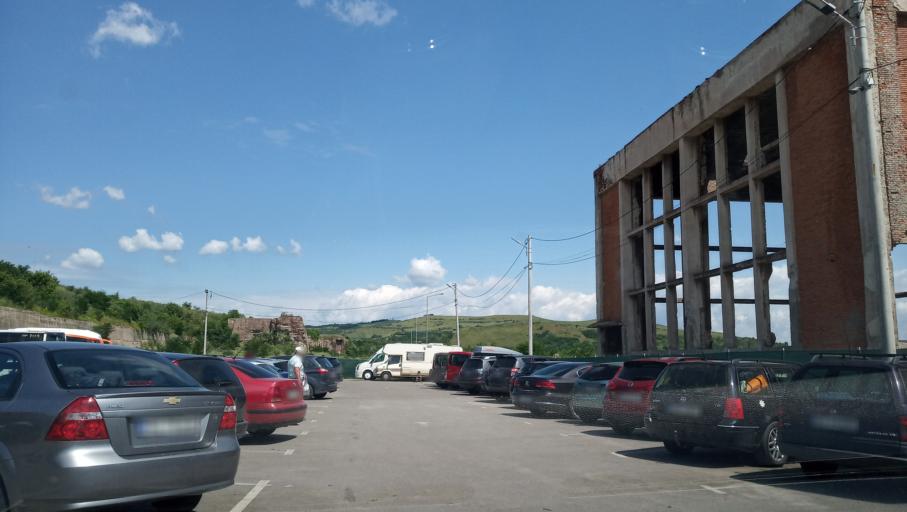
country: RO
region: Hunedoara
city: Hunedoara
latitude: 45.7520
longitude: 22.8890
